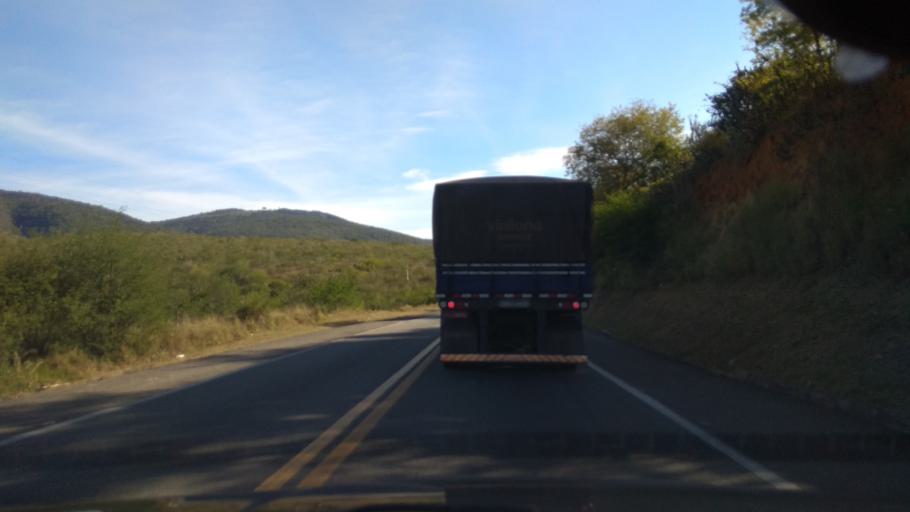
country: BR
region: Bahia
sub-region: Jequie
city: Jequie
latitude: -13.7689
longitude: -40.1023
